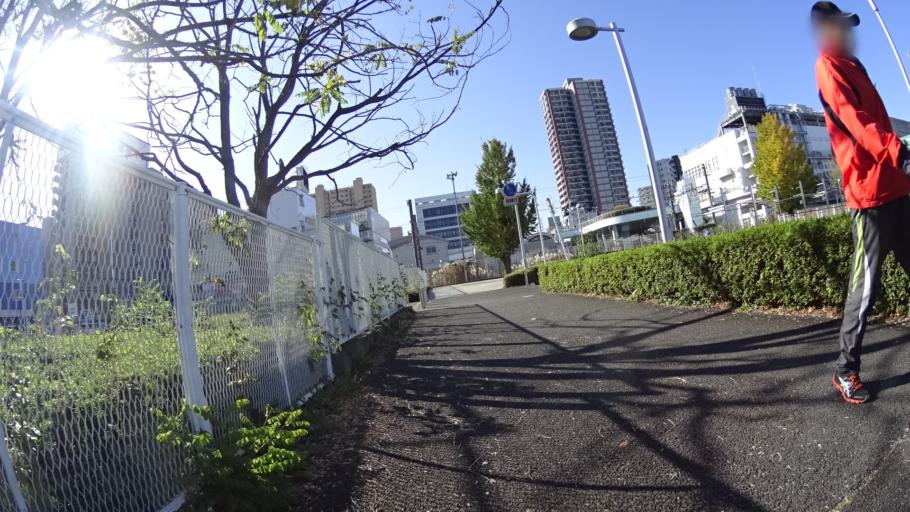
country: JP
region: Tokyo
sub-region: Machida-shi
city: Machida
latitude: 35.5813
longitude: 139.3723
